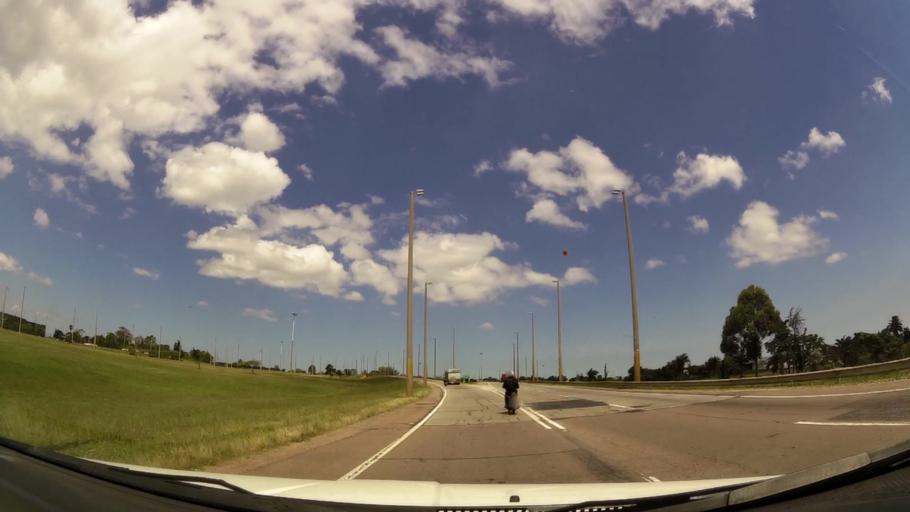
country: UY
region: Canelones
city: La Paz
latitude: -34.8223
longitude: -56.2536
